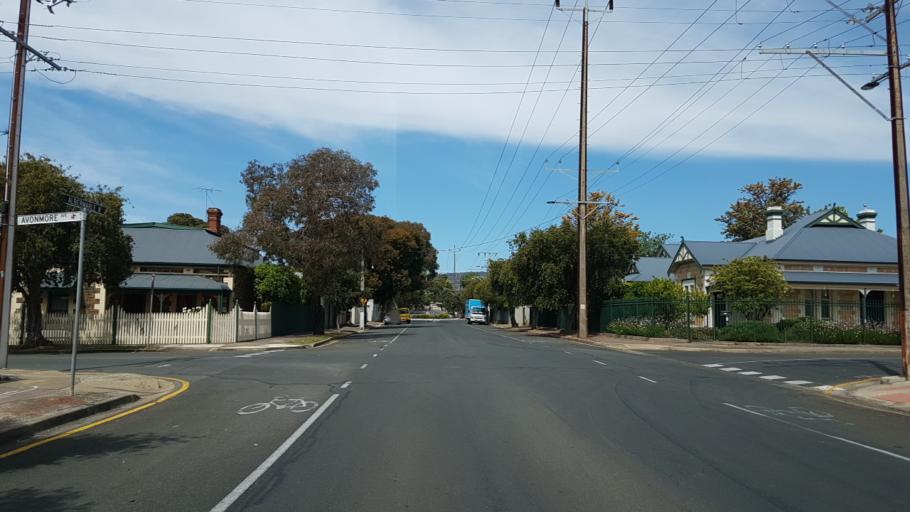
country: AU
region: South Australia
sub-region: Norwood Payneham St Peters
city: Trinity Gardens
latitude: -34.9120
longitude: 138.6447
